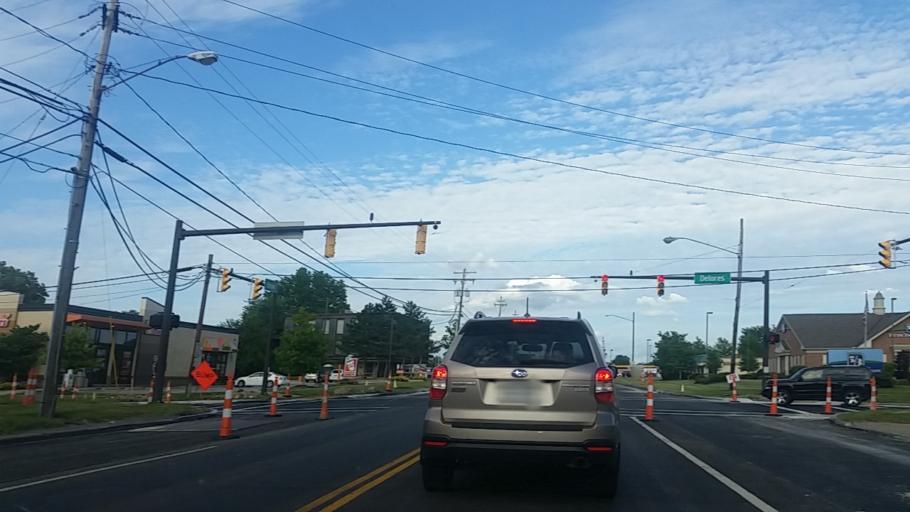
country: US
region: Ohio
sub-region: Cuyahoga County
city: Brook Park
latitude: 41.4039
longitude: -81.8090
